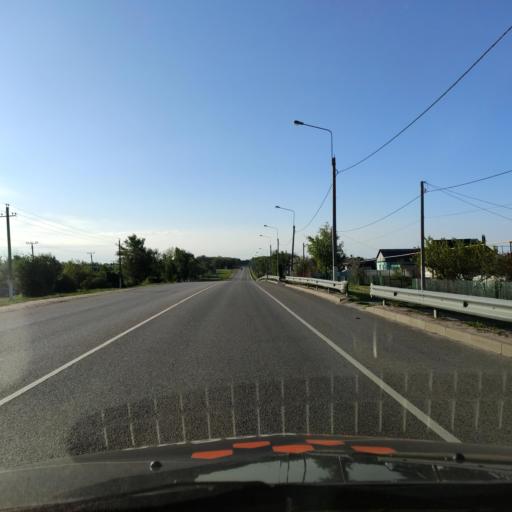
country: RU
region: Lipetsk
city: Yelets
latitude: 52.5548
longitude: 38.7018
